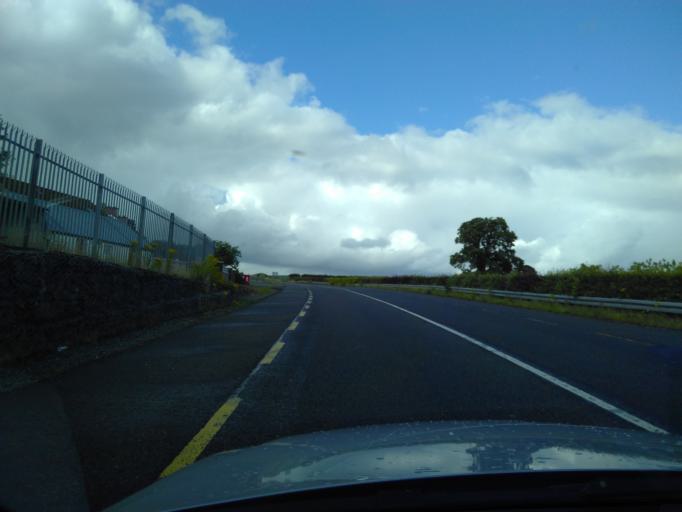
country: IE
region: Ulster
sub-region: County Donegal
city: Ramelton
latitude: 54.9892
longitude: -7.6657
